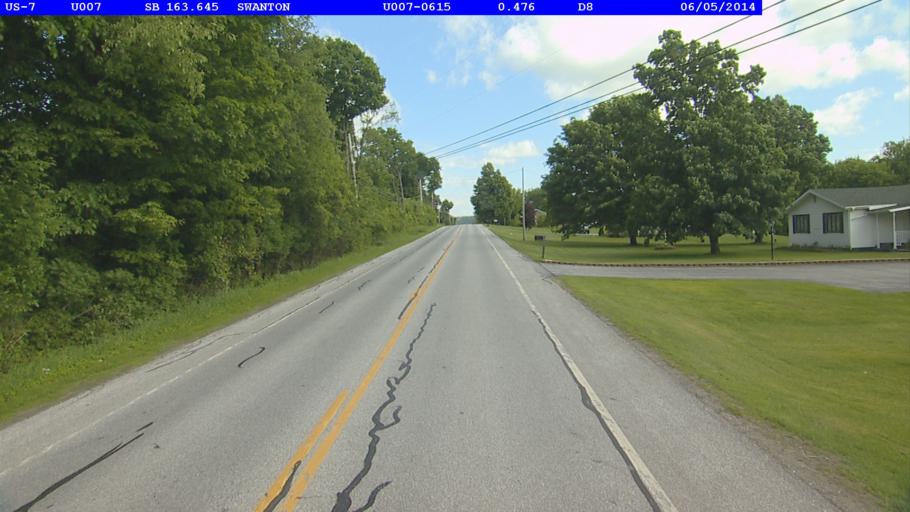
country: US
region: Vermont
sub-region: Franklin County
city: Saint Albans
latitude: 44.8553
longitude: -73.0929
